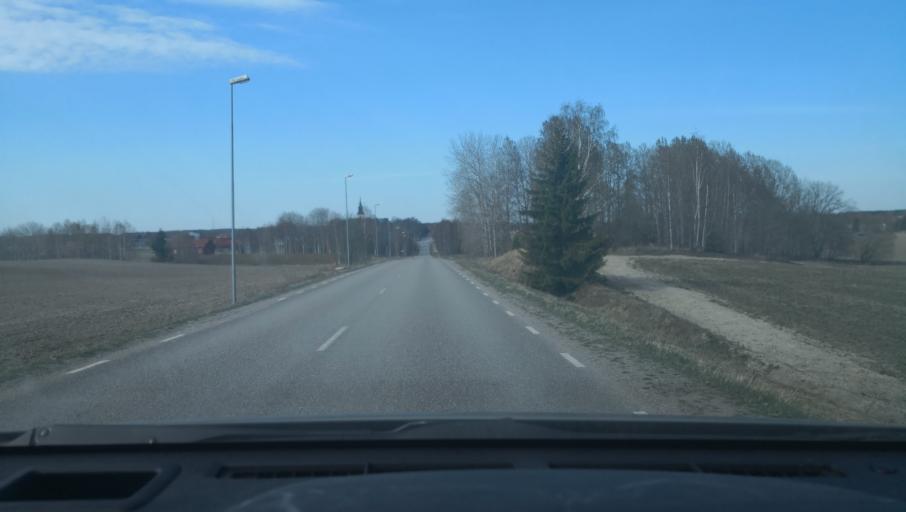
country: SE
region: Uppsala
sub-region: Heby Kommun
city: Heby
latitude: 59.9298
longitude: 16.8560
